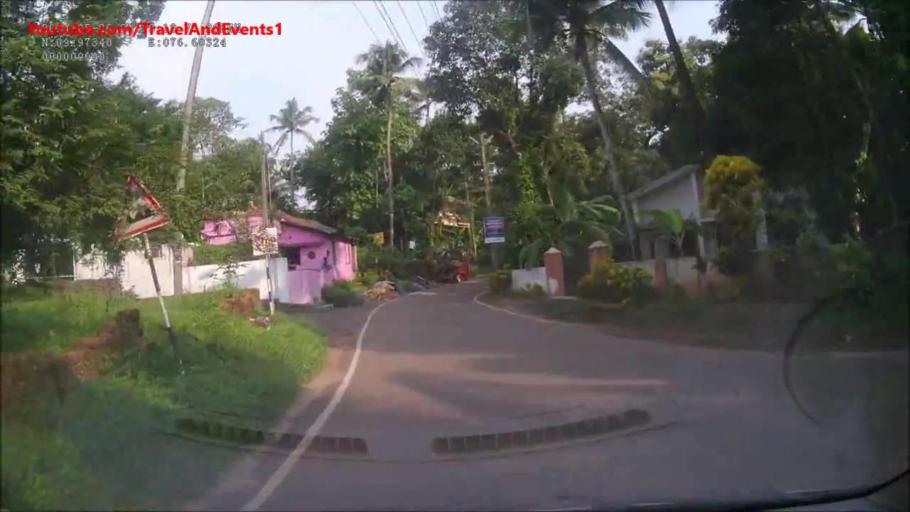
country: IN
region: Kerala
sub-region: Ernakulam
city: Muvattupula
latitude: 9.9668
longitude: 76.6125
